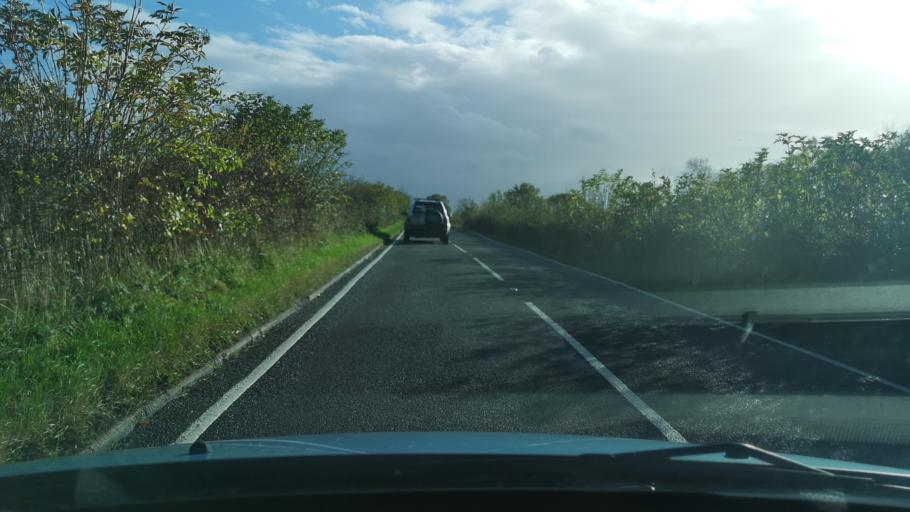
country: GB
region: England
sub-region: City and Borough of Wakefield
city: Crofton
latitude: 53.6434
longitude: -1.4201
